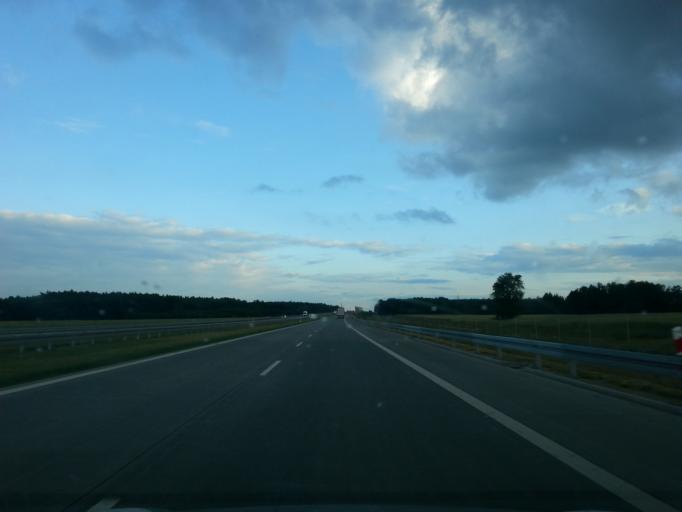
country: PL
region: Lodz Voivodeship
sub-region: Powiat sieradzki
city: Brzeznio
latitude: 51.5164
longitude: 18.6940
